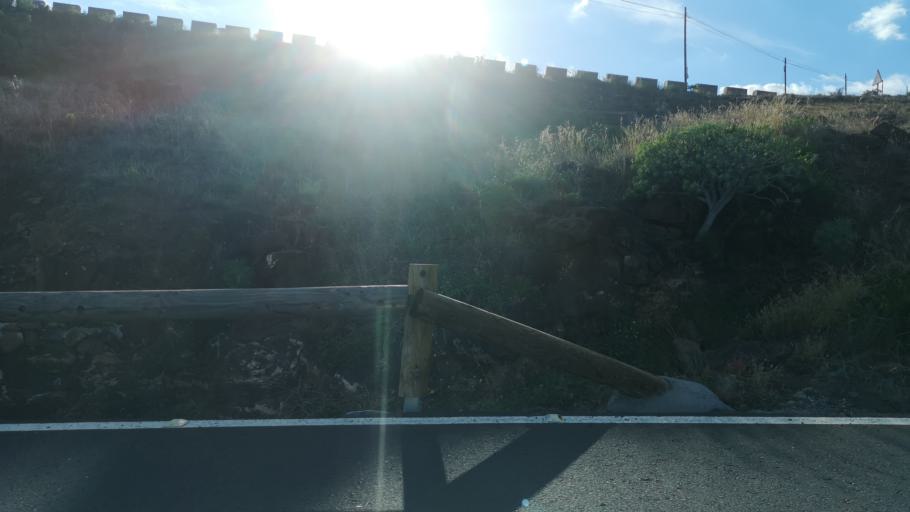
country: ES
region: Canary Islands
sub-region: Provincia de Santa Cruz de Tenerife
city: San Sebastian de la Gomera
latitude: 28.0854
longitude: -17.1372
